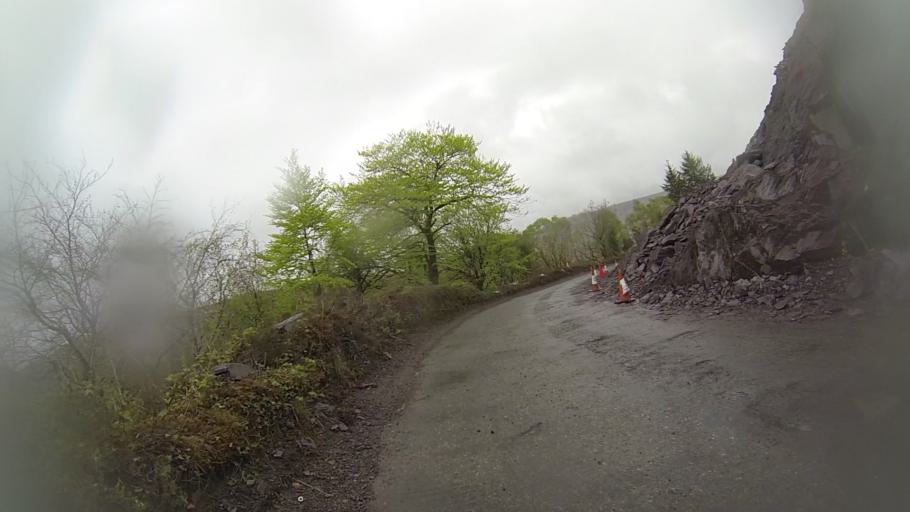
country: IE
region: Munster
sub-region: Ciarrai
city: Kenmare
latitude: 51.8063
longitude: -9.5571
